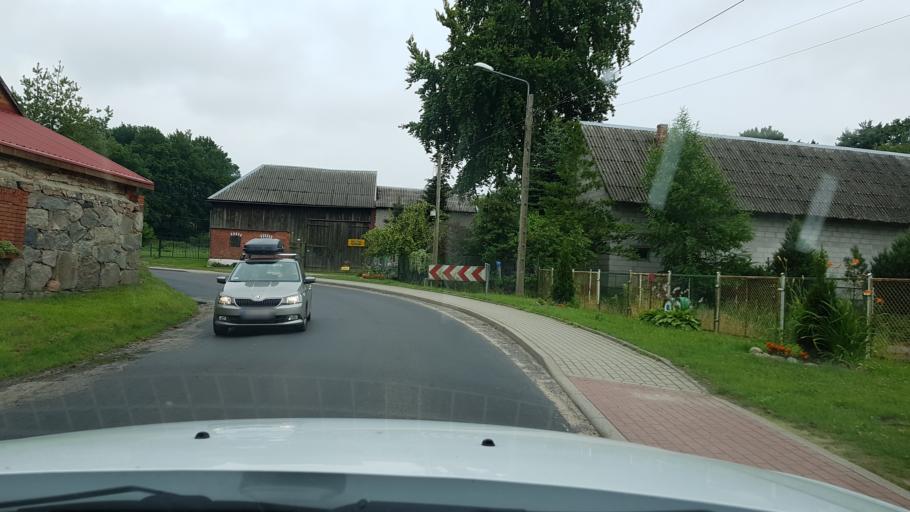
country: PL
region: West Pomeranian Voivodeship
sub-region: Powiat slawienski
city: Slawno
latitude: 54.4883
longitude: 16.5822
